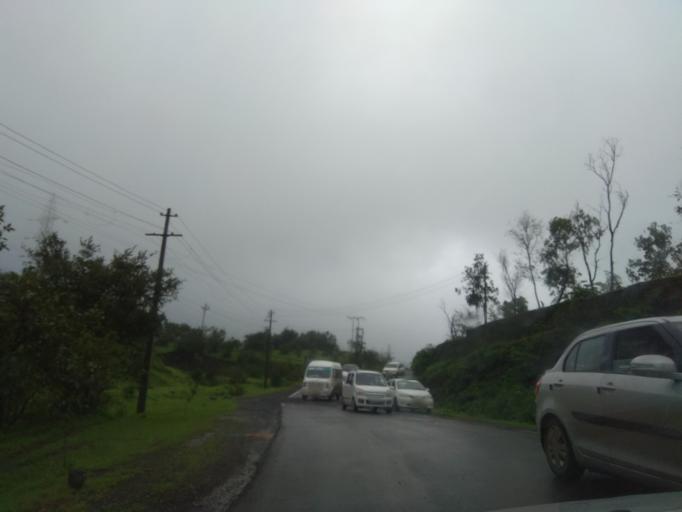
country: IN
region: Maharashtra
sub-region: Raigarh
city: Indapur
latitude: 18.4921
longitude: 73.4216
